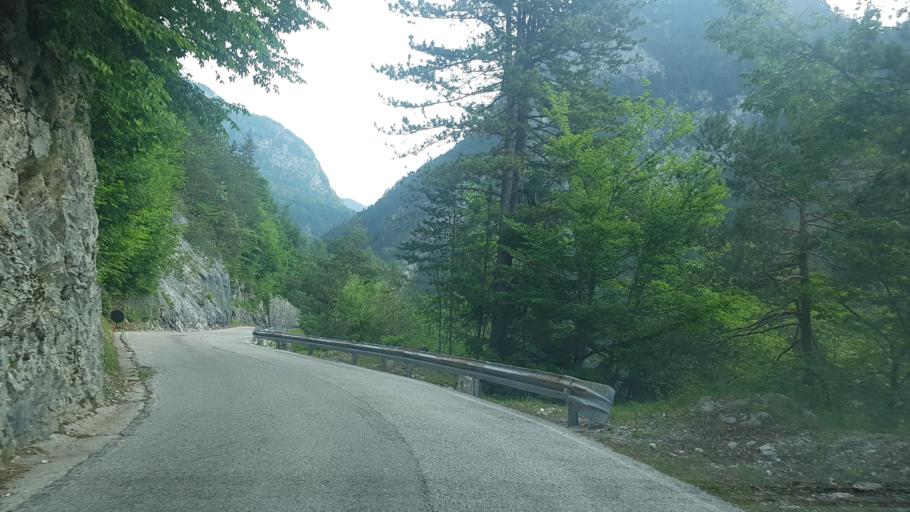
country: IT
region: Friuli Venezia Giulia
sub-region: Provincia di Udine
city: Pontebba
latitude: 46.5203
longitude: 13.2998
